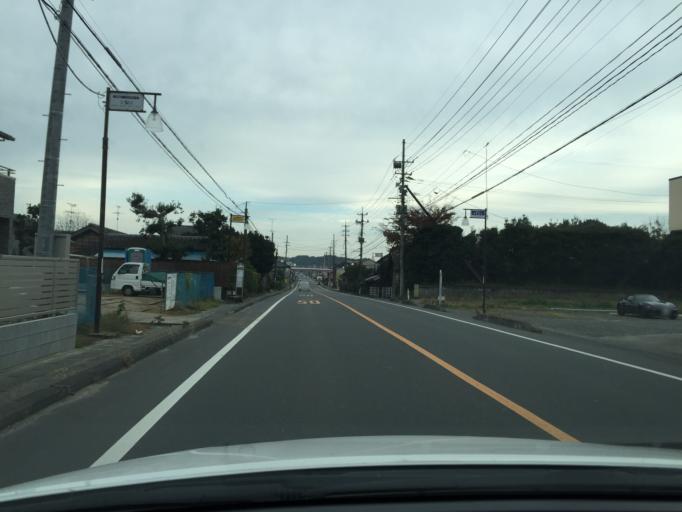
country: JP
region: Fukushima
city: Iwaki
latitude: 37.0678
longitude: 140.8486
